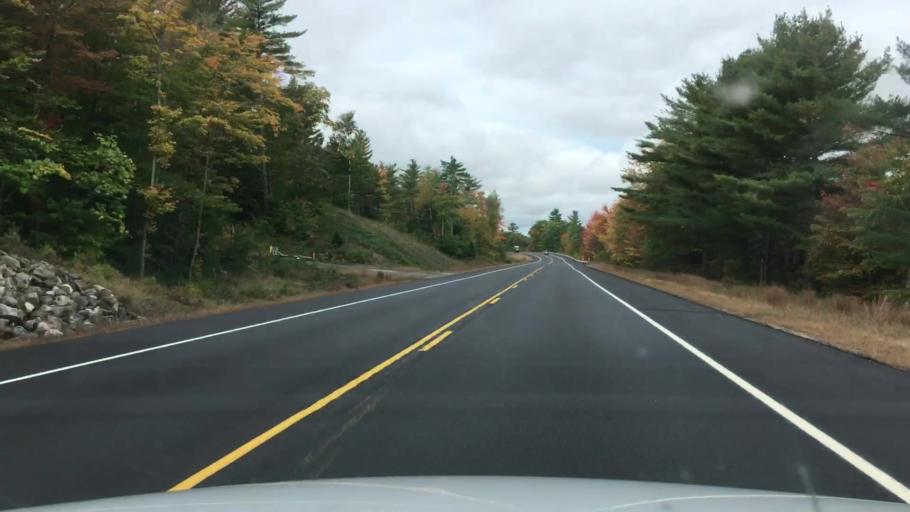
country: US
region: Maine
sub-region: Oxford County
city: Bethel
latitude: 44.3978
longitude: -70.9421
